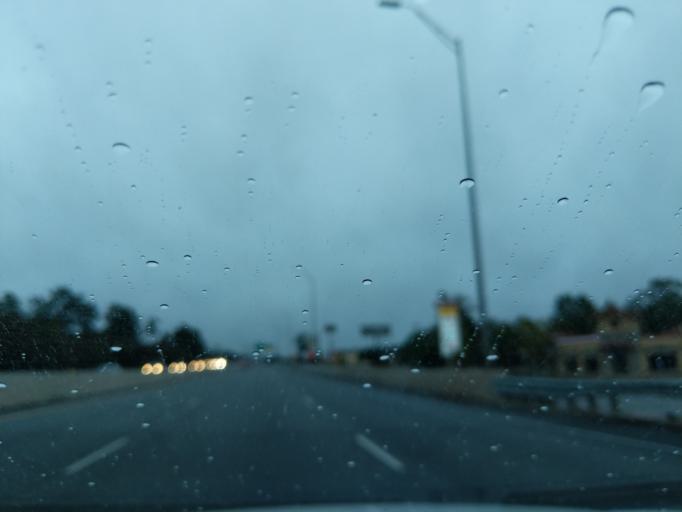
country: US
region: Texas
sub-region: Angelina County
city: Lufkin
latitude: 31.3134
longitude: -94.7180
